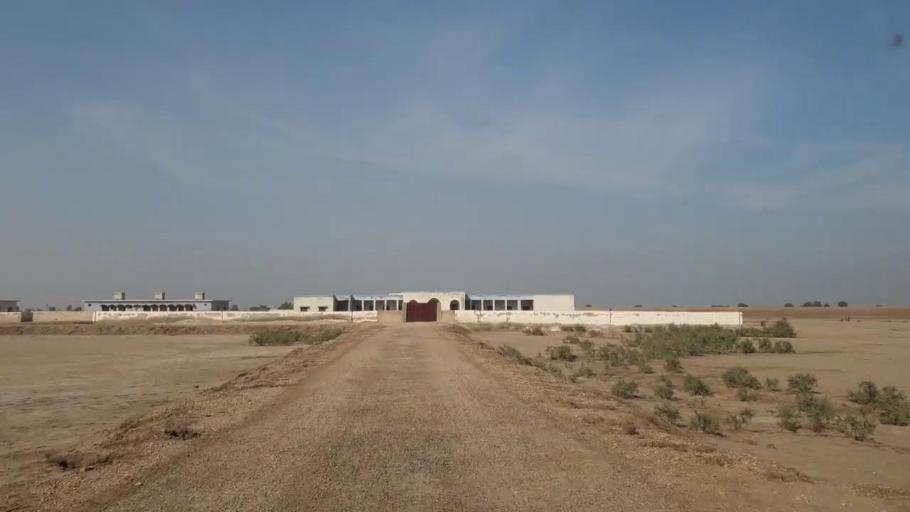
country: PK
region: Sindh
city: Sann
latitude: 25.9130
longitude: 68.2313
